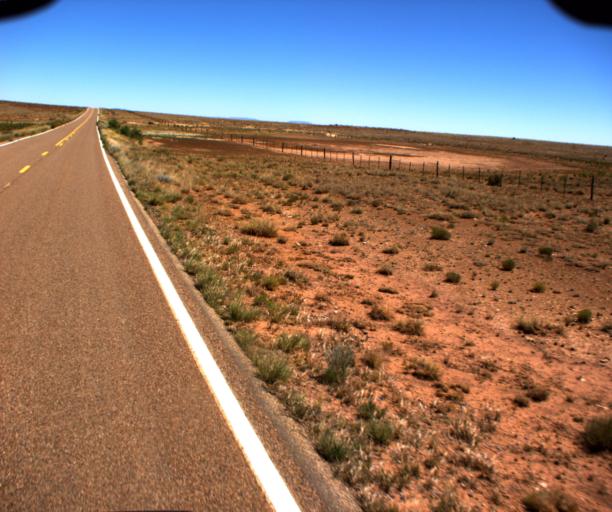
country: US
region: Arizona
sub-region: Navajo County
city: Winslow
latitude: 34.8570
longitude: -110.6634
